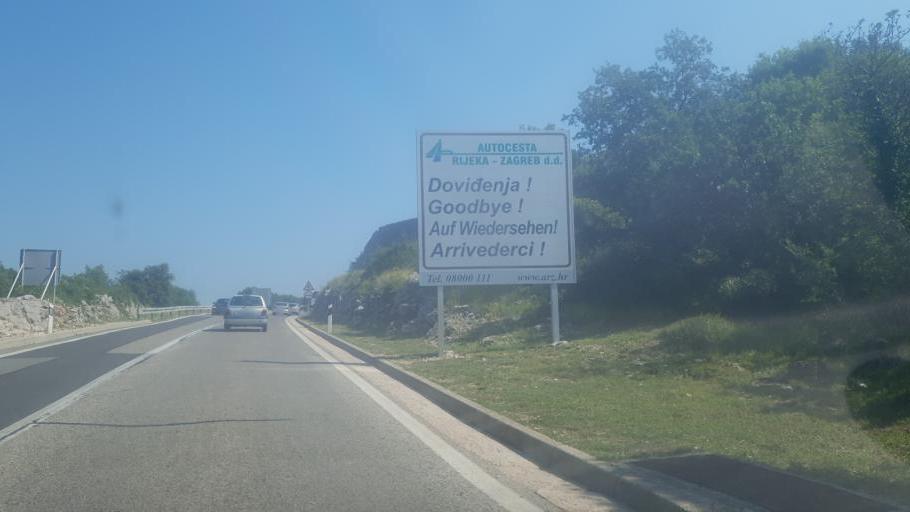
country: HR
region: Primorsko-Goranska
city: Kraljevica
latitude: 45.2538
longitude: 14.5792
